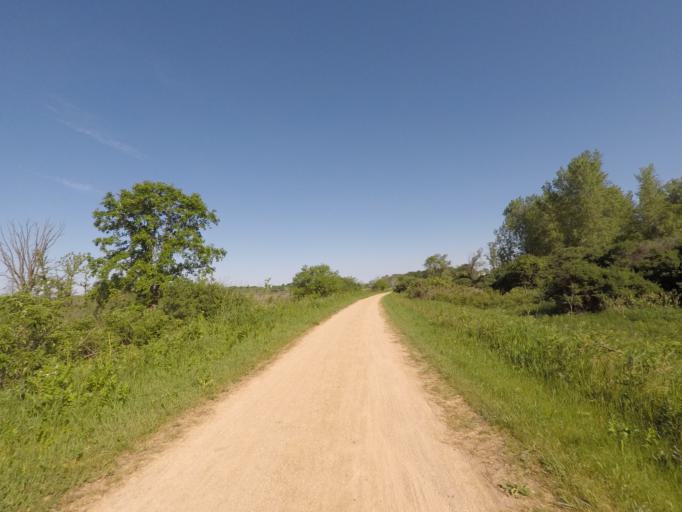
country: US
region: Wisconsin
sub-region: Dane County
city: Verona
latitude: 42.9813
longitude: -89.5605
